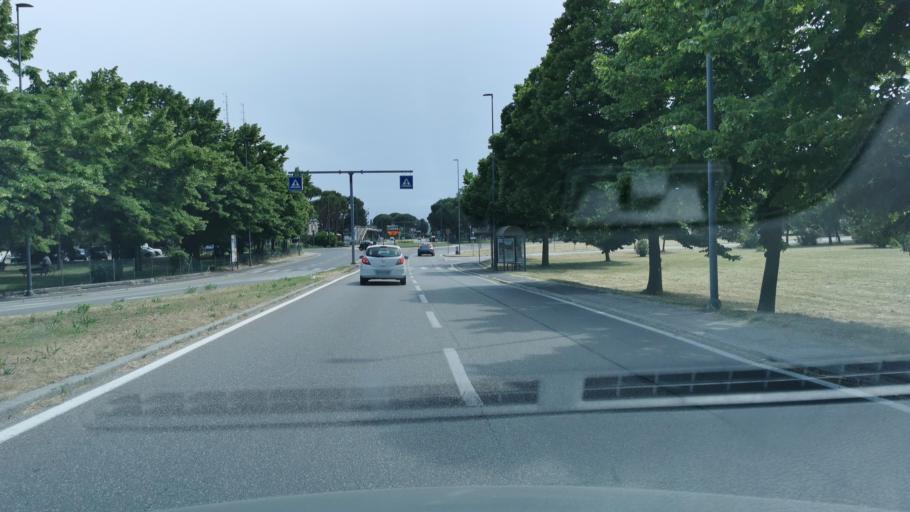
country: IT
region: Emilia-Romagna
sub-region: Provincia di Ravenna
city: Ravenna
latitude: 44.4261
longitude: 12.1828
